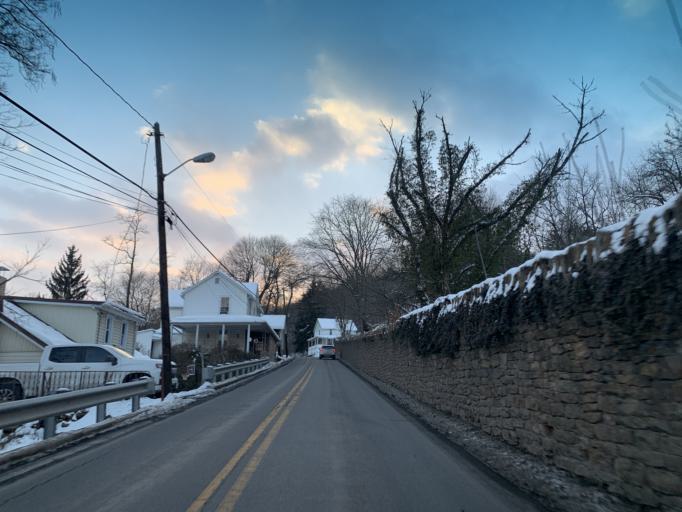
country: US
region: Maryland
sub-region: Allegany County
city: Frostburg
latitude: 39.6949
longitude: -78.8822
